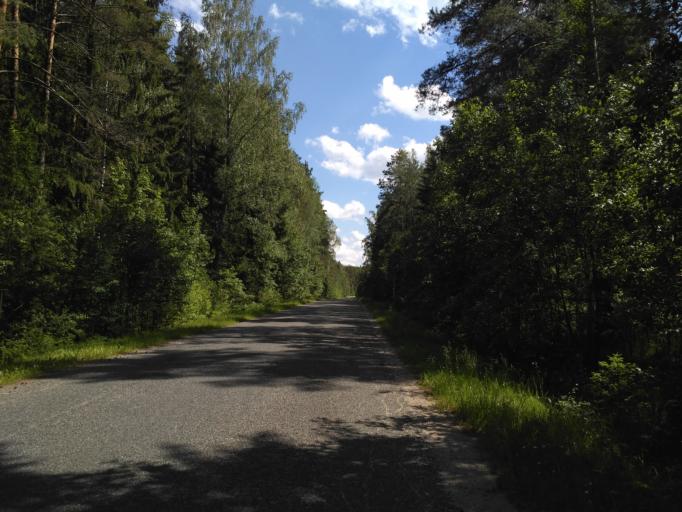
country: BY
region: Minsk
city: Horad Barysaw
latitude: 54.0299
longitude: 28.6340
